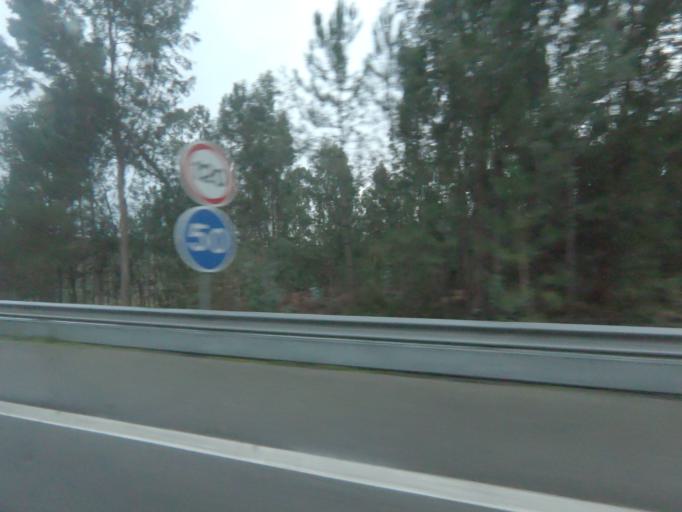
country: PT
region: Braga
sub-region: Vila Verde
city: Prado
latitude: 41.5432
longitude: -8.4983
